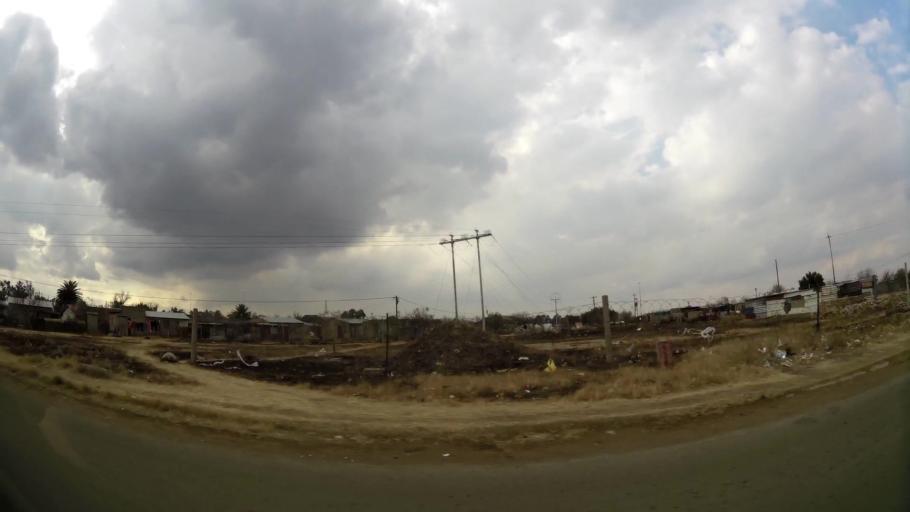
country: ZA
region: Orange Free State
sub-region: Fezile Dabi District Municipality
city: Sasolburg
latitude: -26.8529
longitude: 27.8699
